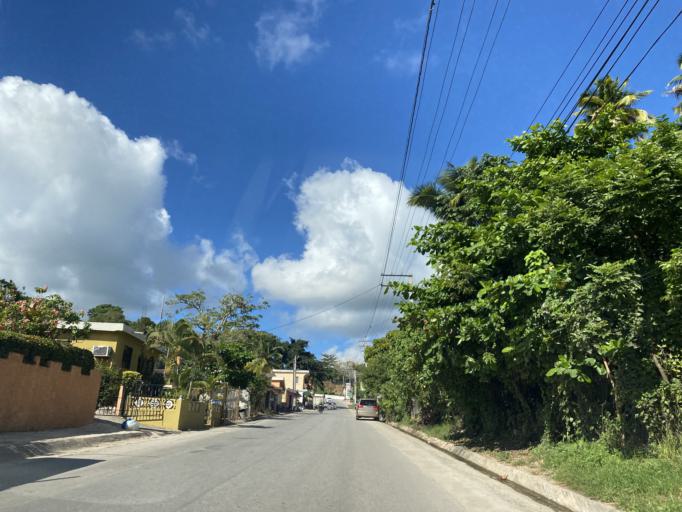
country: DO
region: Samana
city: Samana
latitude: 19.2107
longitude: -69.3552
